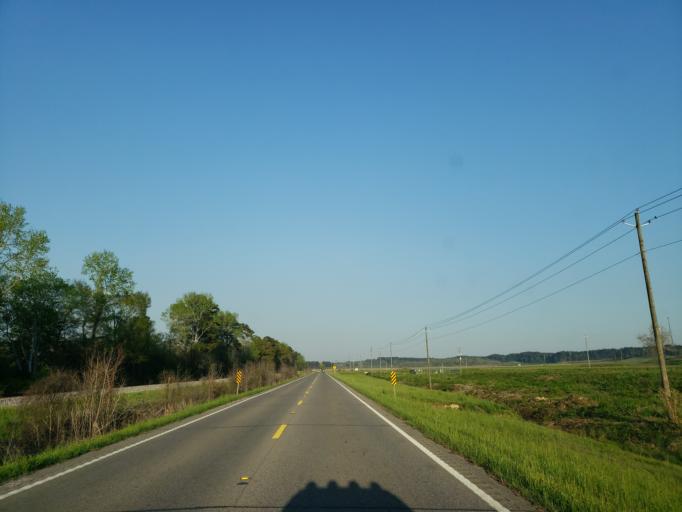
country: US
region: Mississippi
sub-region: Lauderdale County
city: Marion
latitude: 32.3941
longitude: -88.6353
